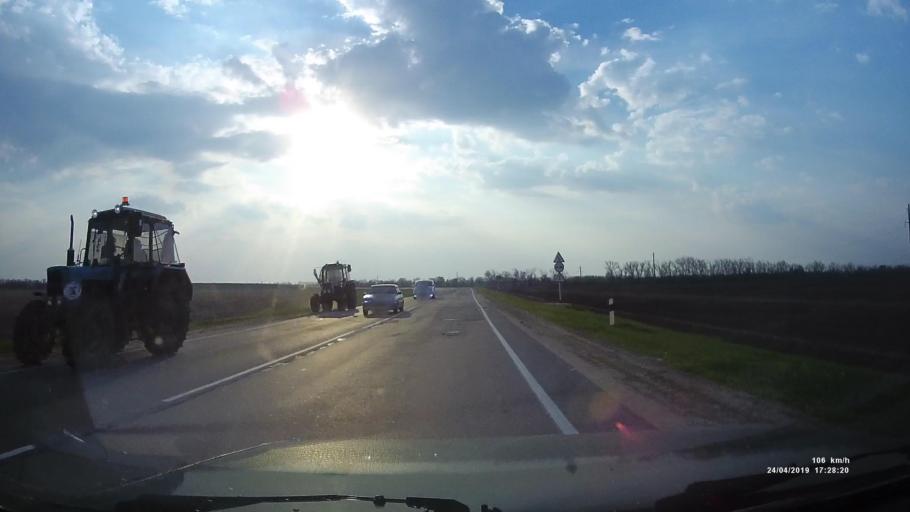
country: RU
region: Rostov
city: Tselina
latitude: 46.5320
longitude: 41.1797
